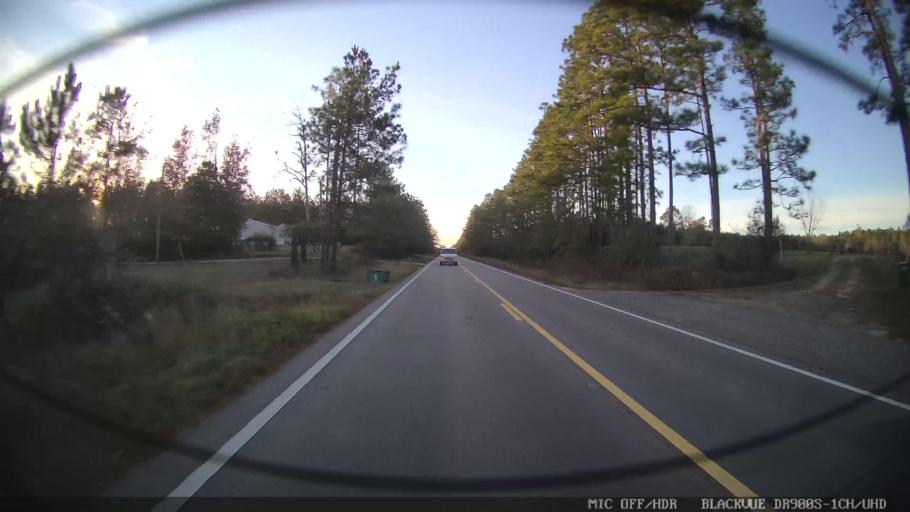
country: US
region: Mississippi
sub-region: Lamar County
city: Lumberton
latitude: 30.9989
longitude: -89.3016
